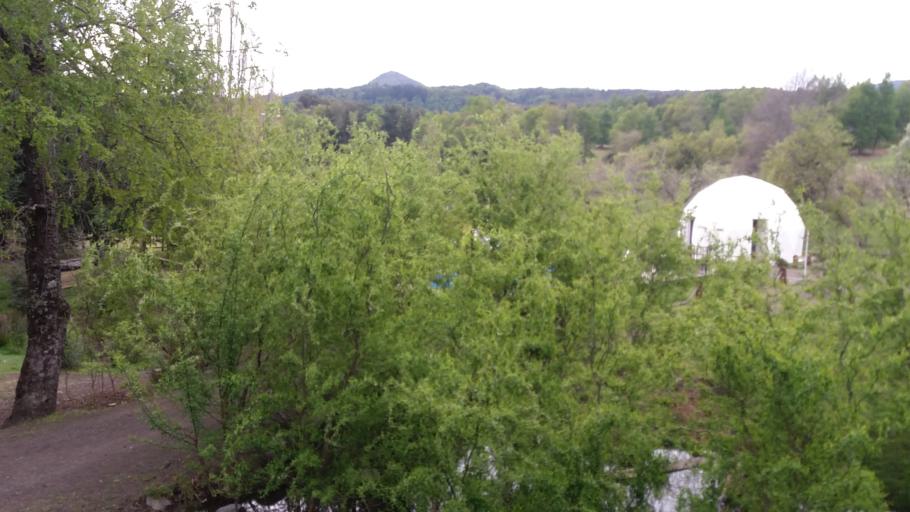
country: CL
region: Araucania
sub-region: Provincia de Cautin
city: Pucon
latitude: -38.8323
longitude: -71.6922
